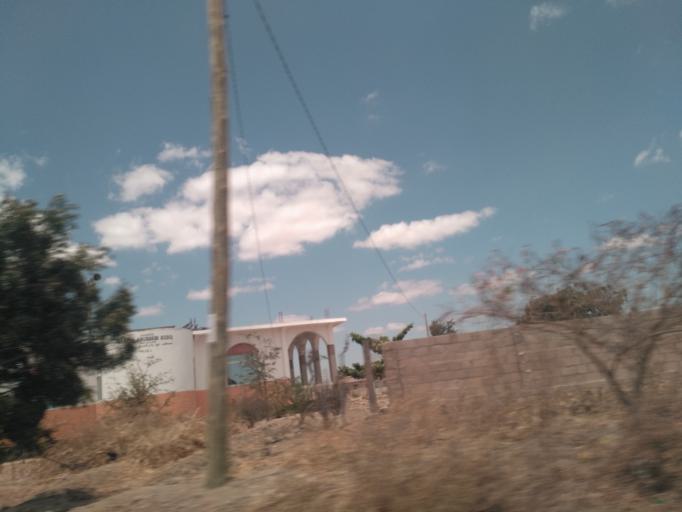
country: TZ
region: Dodoma
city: Kisasa
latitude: -6.1713
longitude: 35.7941
